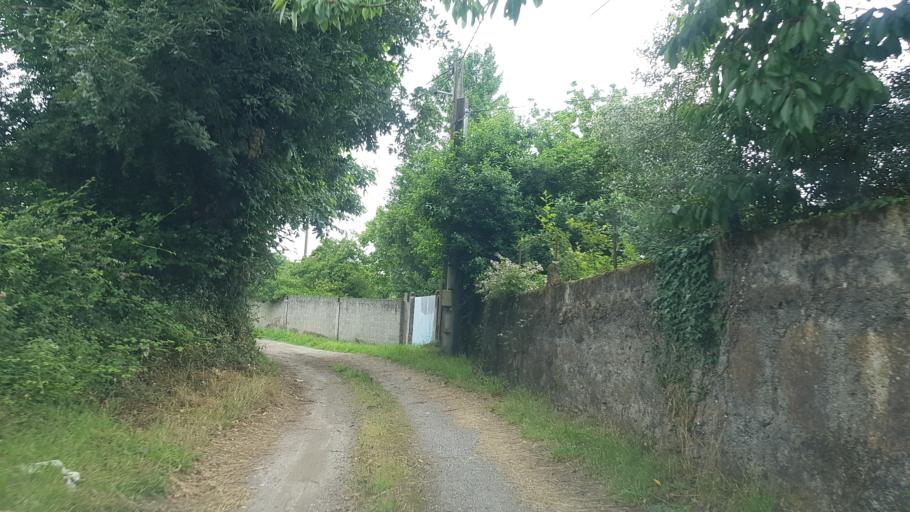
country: ES
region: Galicia
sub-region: Provincia de Lugo
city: Lugo
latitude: 43.0312
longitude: -7.5401
